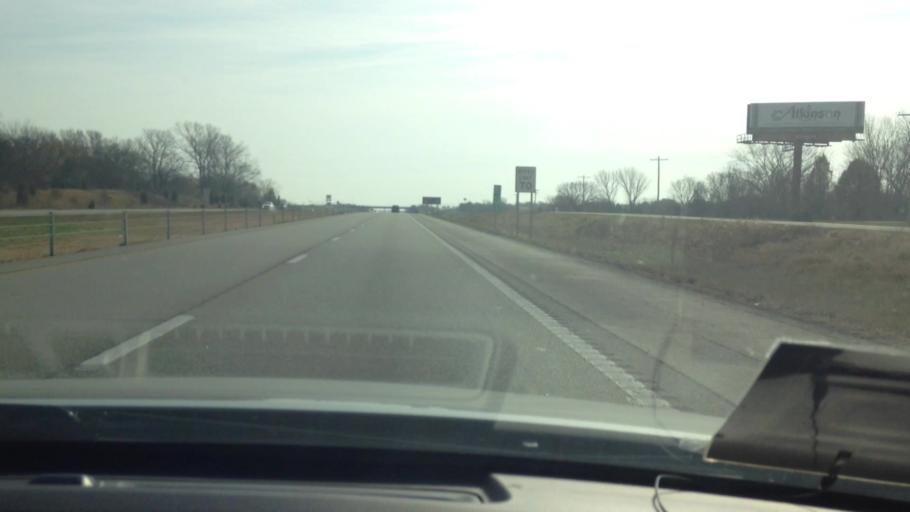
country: US
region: Missouri
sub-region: Cass County
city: Peculiar
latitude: 38.7314
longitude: -94.4646
